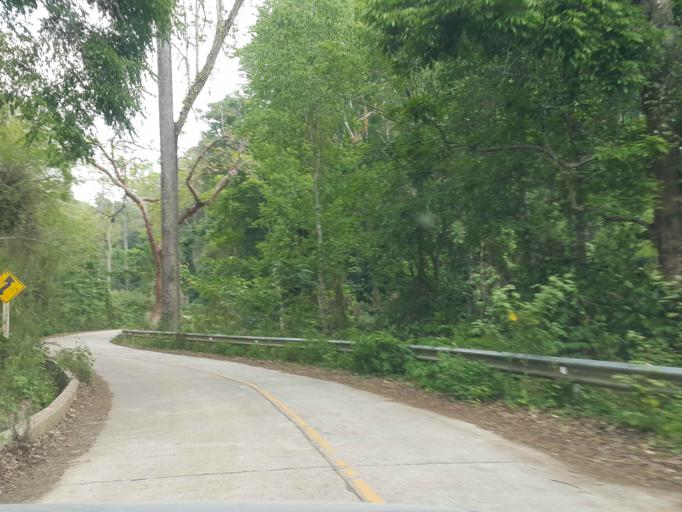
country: TH
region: Chiang Mai
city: Wiang Haeng
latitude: 19.3792
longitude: 98.7452
